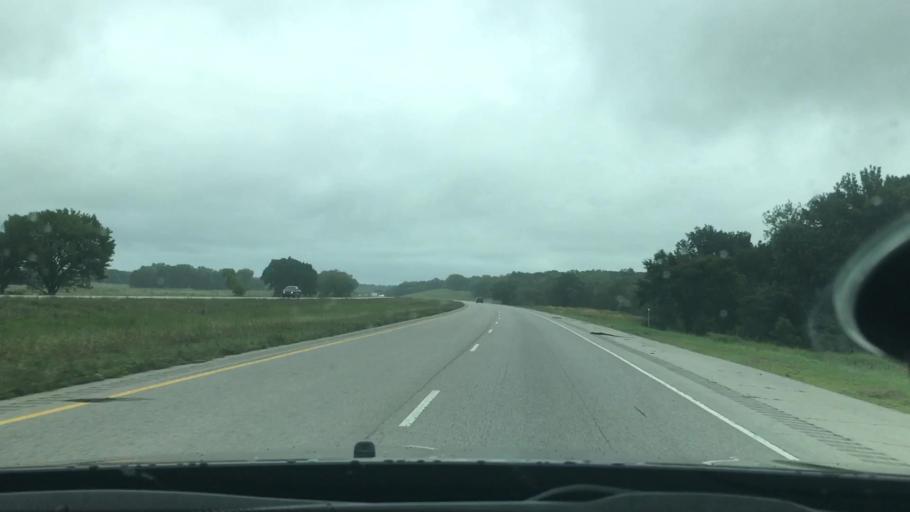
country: US
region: Oklahoma
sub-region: Okfuskee County
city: Boley
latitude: 35.3861
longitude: -96.4228
